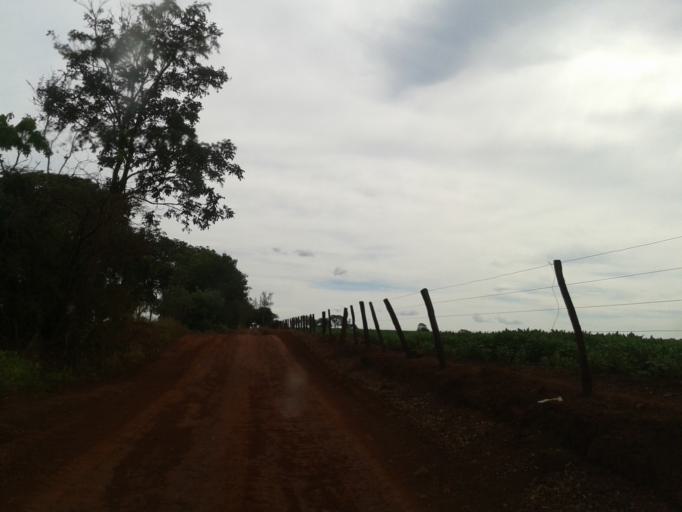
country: BR
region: Minas Gerais
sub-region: Centralina
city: Centralina
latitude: -18.6741
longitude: -49.3545
